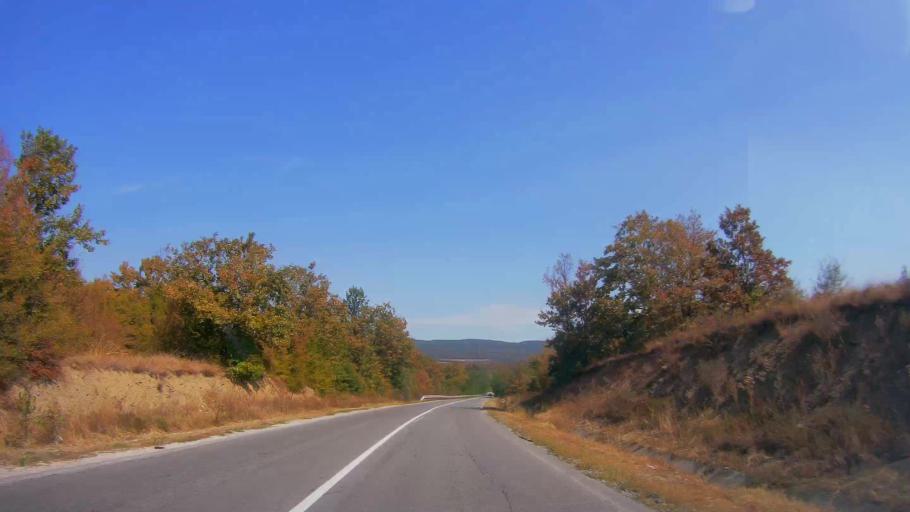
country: BG
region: Shumen
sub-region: Obshtina Smyadovo
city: Smyadovo
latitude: 42.9641
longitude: 26.9504
